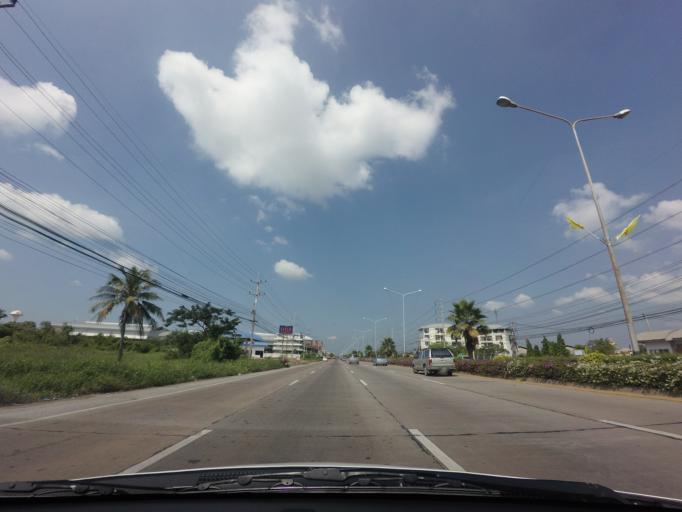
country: TH
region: Nakhon Pathom
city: Sam Phran
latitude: 13.7478
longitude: 100.2037
